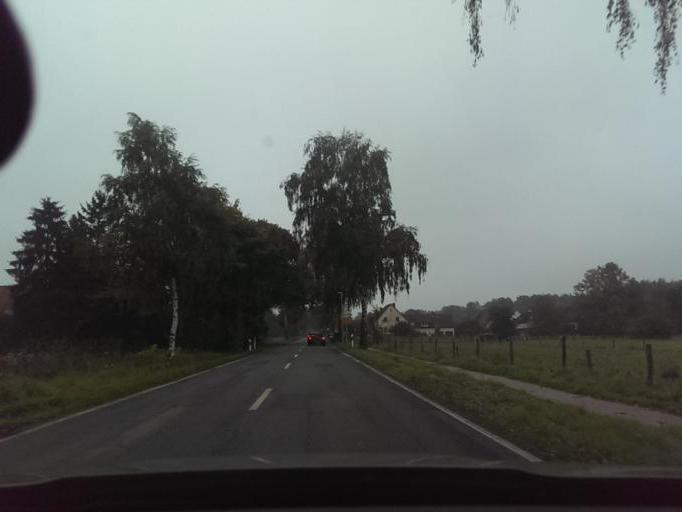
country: DE
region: Lower Saxony
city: Garbsen-Mitte
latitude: 52.5067
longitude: 9.6398
